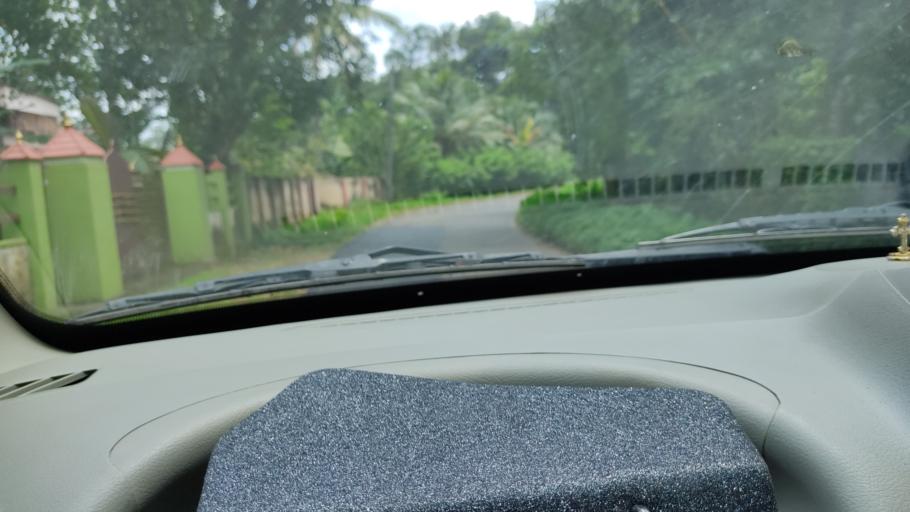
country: IN
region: Kerala
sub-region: Pattanamtitta
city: Tiruvalla
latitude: 9.3312
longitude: 76.5230
